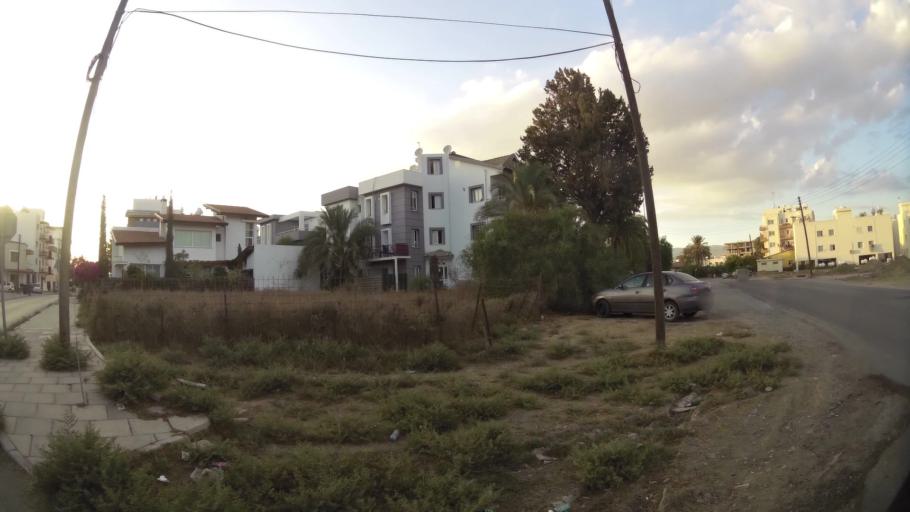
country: CY
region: Lefkosia
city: Nicosia
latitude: 35.1929
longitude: 33.3733
